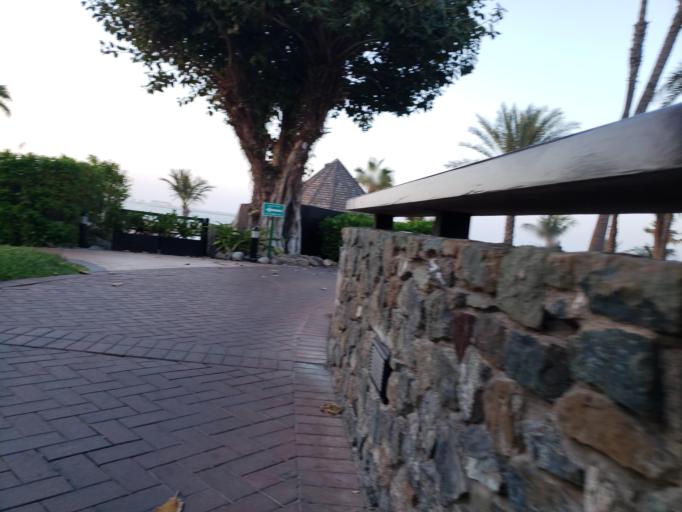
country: AE
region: Dubai
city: Dubai
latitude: 24.9876
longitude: 55.0213
